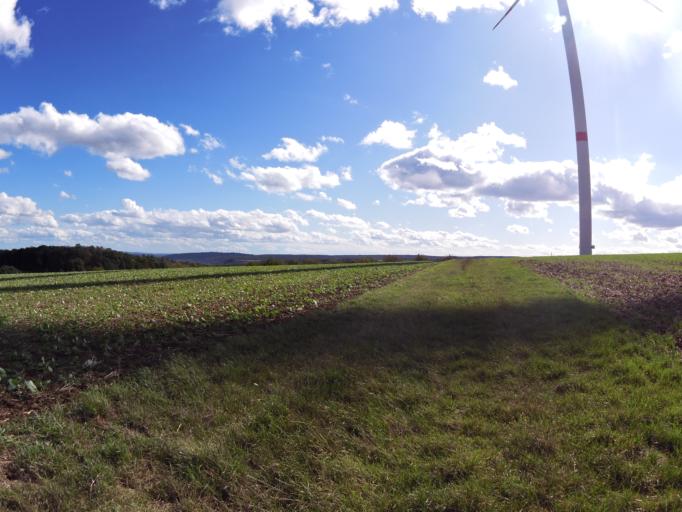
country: DE
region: Bavaria
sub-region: Regierungsbezirk Unterfranken
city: Erlabrunn
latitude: 49.8338
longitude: 9.8341
